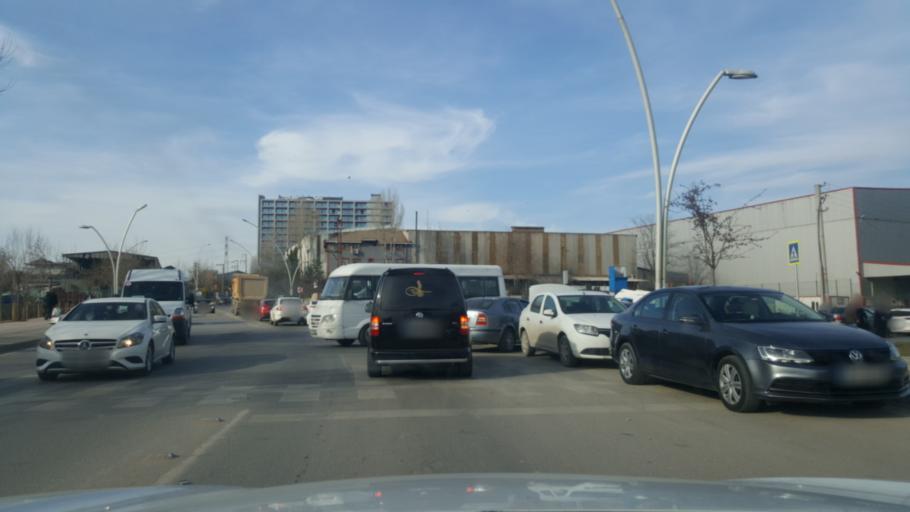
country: TR
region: Kocaeli
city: Gebze
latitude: 40.7905
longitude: 29.4422
